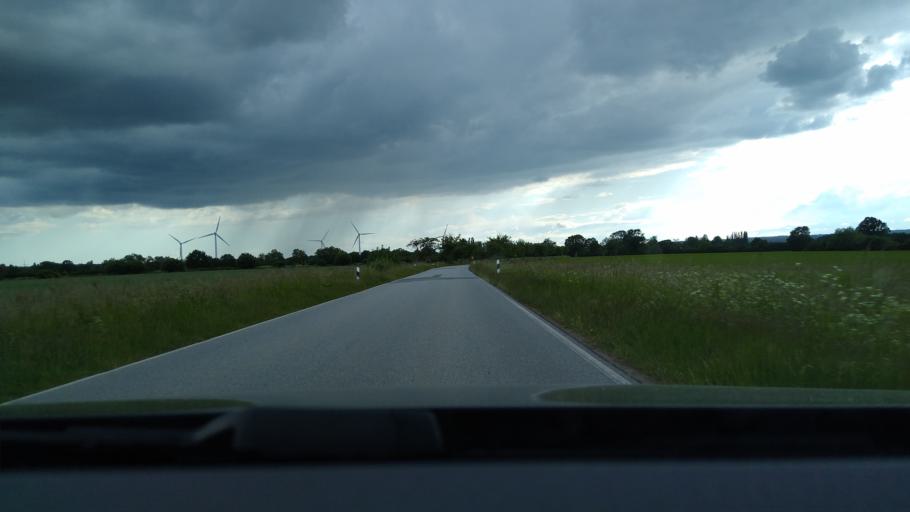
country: DE
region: Schleswig-Holstein
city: Riepsdorf
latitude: 54.2160
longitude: 10.9528
